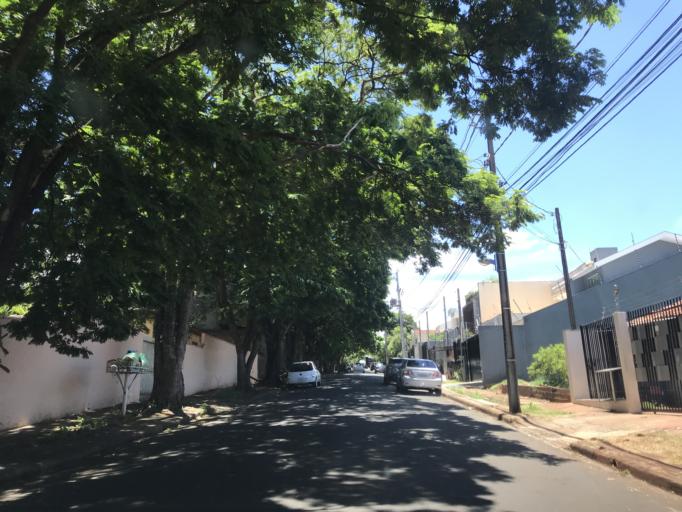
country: BR
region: Parana
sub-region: Maringa
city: Maringa
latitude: -23.4475
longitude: -51.9445
